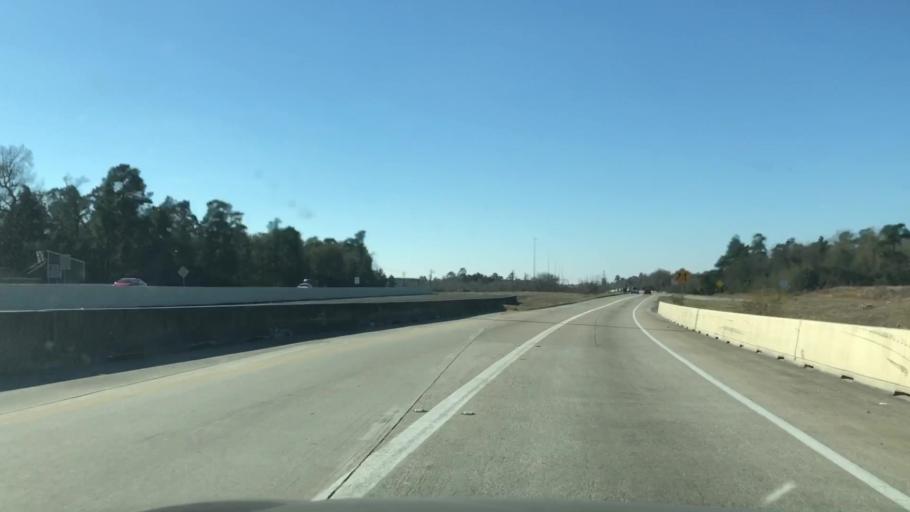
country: US
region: Texas
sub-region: Harris County
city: Jacinto City
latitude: 29.8132
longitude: -95.2102
